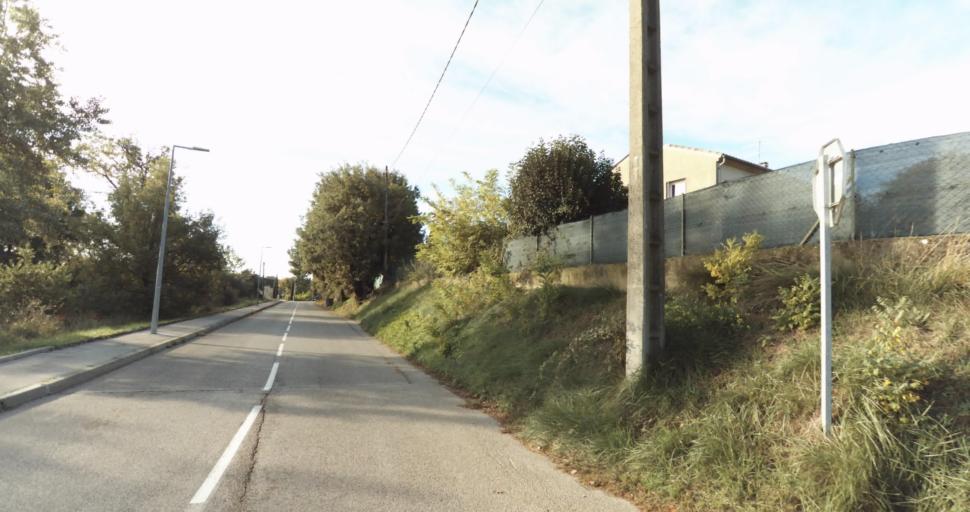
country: FR
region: Provence-Alpes-Cote d'Azur
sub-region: Departement des Bouches-du-Rhone
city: Venelles
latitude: 43.5894
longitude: 5.4750
